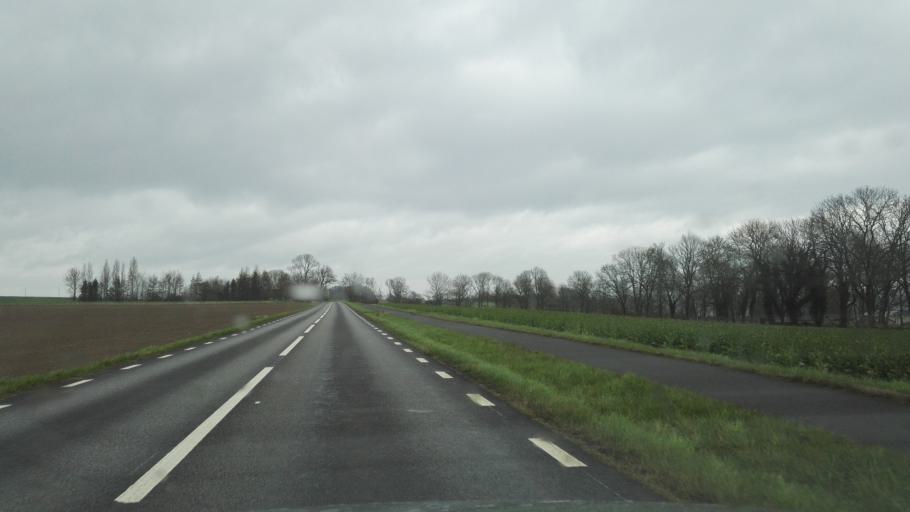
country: SE
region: Skane
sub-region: Simrishamns Kommun
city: Simrishamn
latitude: 55.5024
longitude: 14.3254
